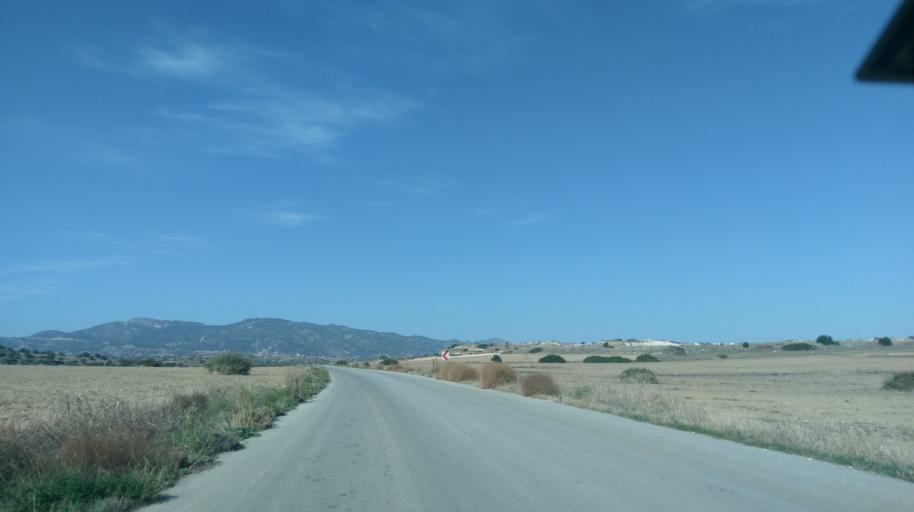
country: CY
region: Ammochostos
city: Trikomo
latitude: 35.3121
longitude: 33.8933
